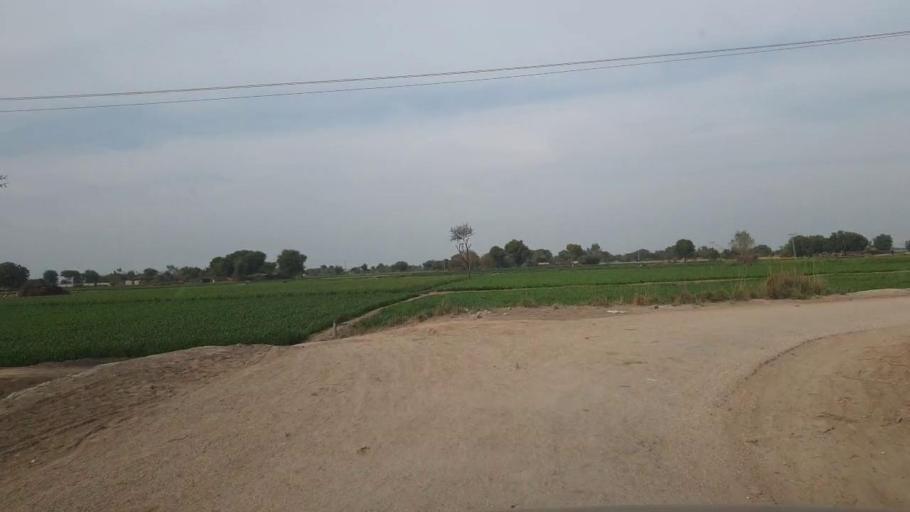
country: PK
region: Sindh
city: Shahpur Chakar
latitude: 26.1108
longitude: 68.5191
